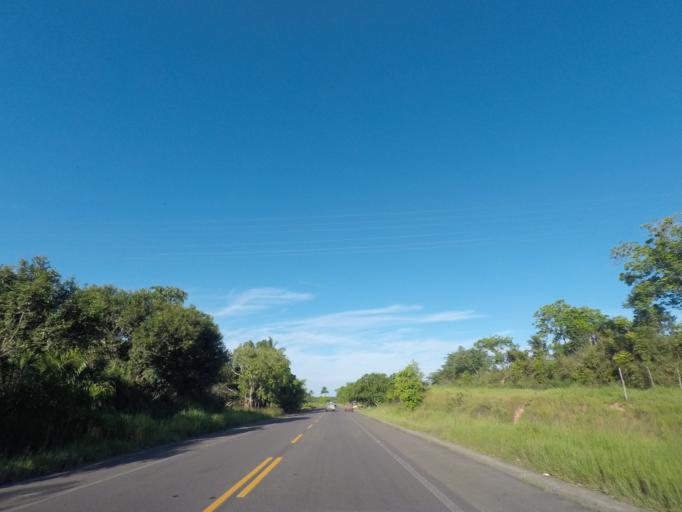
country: BR
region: Bahia
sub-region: Nazare
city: Nazare
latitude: -13.0092
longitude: -38.9709
